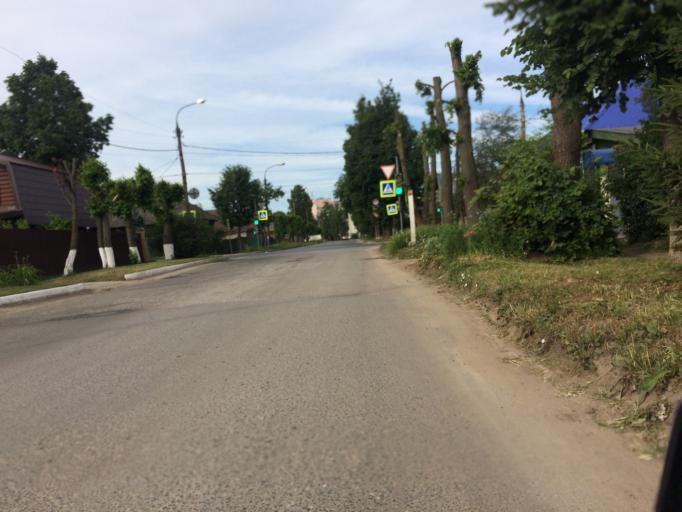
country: RU
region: Mariy-El
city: Yoshkar-Ola
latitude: 56.6470
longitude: 47.9073
